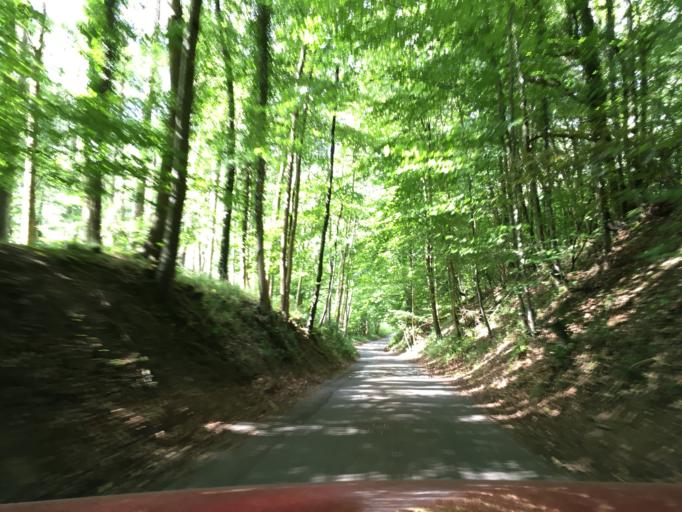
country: GB
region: England
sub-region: Gloucestershire
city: Coates
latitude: 51.7550
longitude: -2.0716
